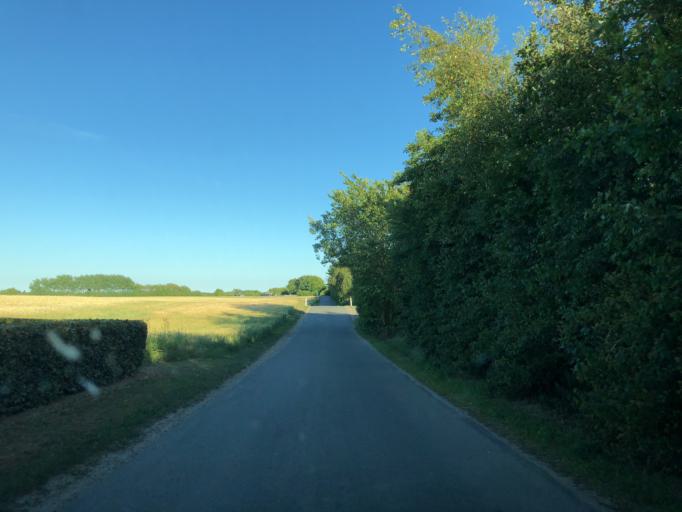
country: DK
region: Central Jutland
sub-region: Horsens Kommune
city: Horsens
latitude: 55.9688
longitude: 9.8117
